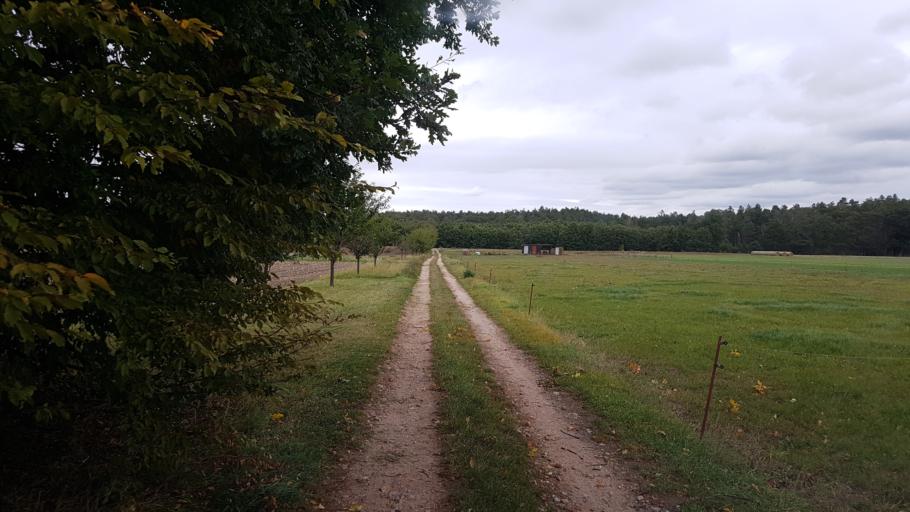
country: DE
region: Brandenburg
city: Doberlug-Kirchhain
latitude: 51.6208
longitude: 13.5953
